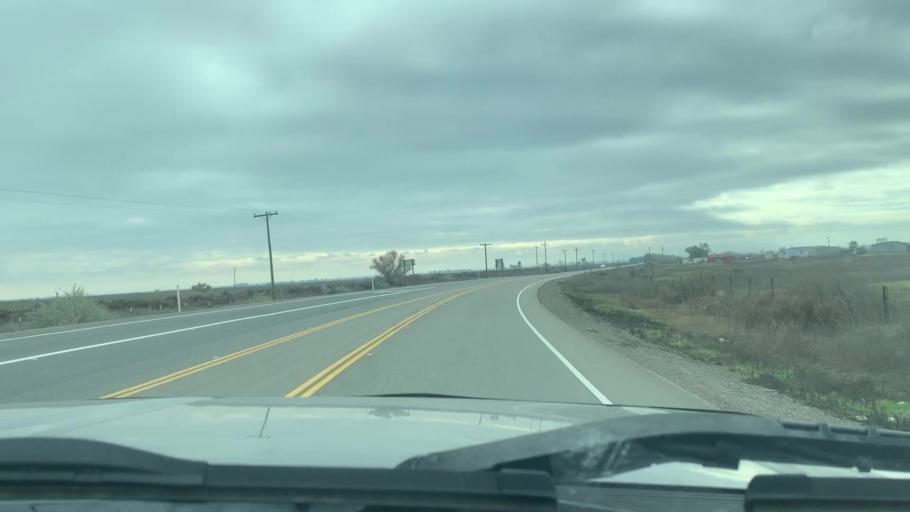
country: US
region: California
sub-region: Merced County
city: Los Banos
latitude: 37.1459
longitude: -120.8252
